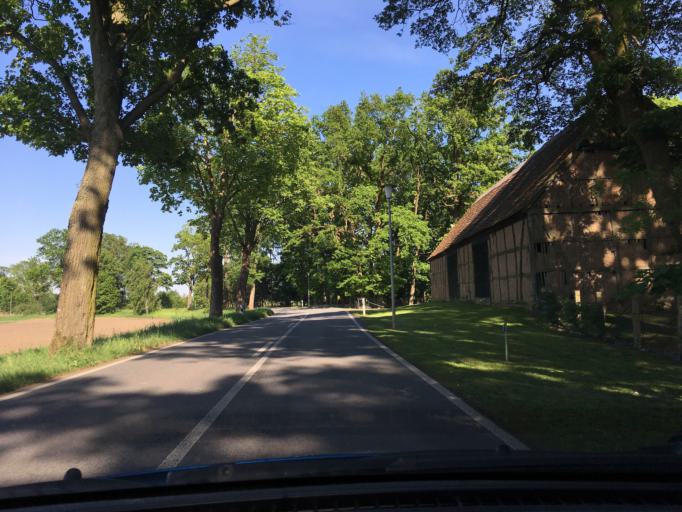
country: DE
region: Brandenburg
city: Lenzen
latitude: 53.0810
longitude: 11.4139
